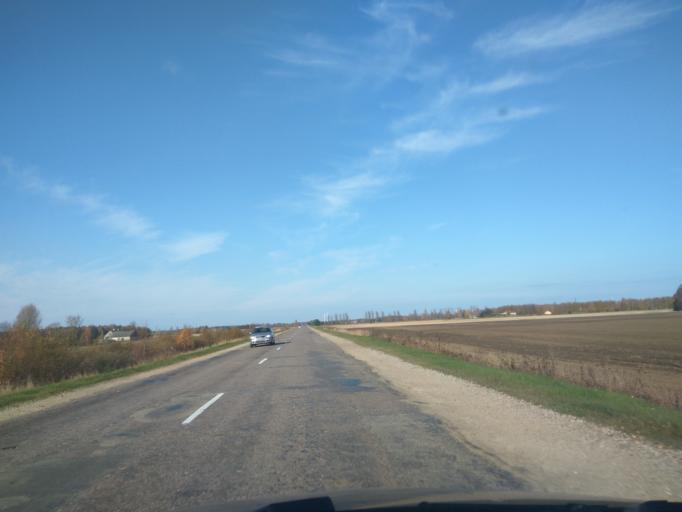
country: LV
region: Ventspils Rajons
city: Piltene
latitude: 57.2448
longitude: 21.5948
